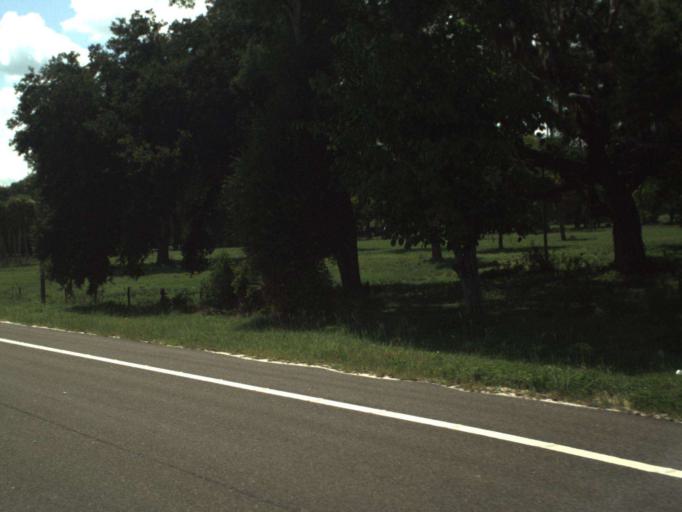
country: US
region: Florida
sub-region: Lake County
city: Mascotte
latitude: 28.5790
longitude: -81.9782
